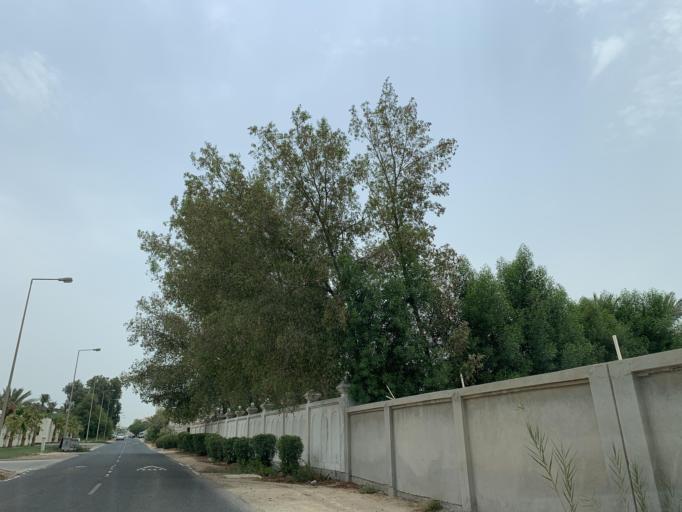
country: BH
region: Northern
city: Madinat `Isa
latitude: 26.1872
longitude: 50.4690
